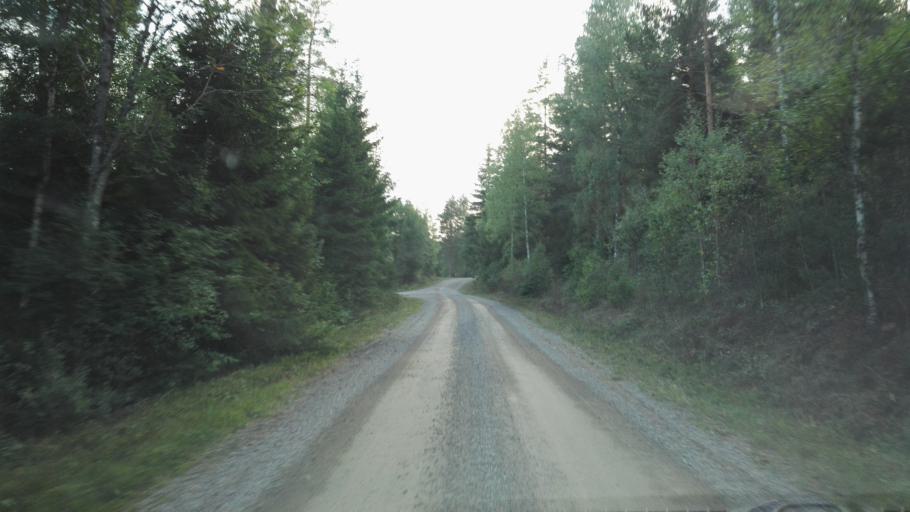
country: SE
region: Joenkoeping
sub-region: Vetlanda Kommun
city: Landsbro
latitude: 57.2594
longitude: 14.9071
